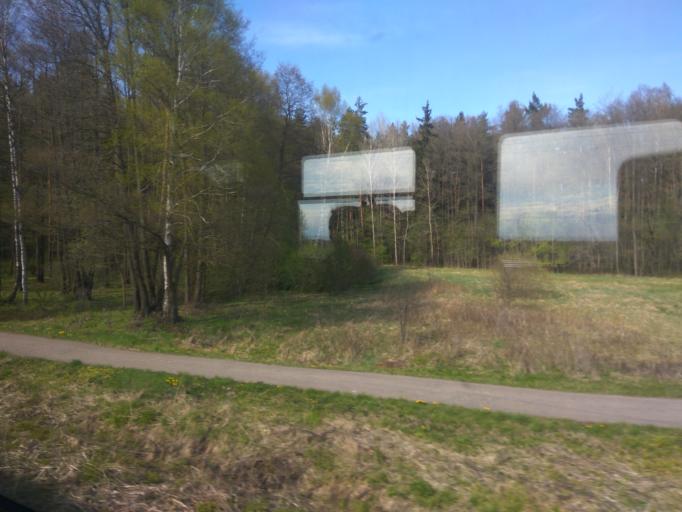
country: LV
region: Babite
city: Pinki
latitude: 56.9692
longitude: 23.8964
